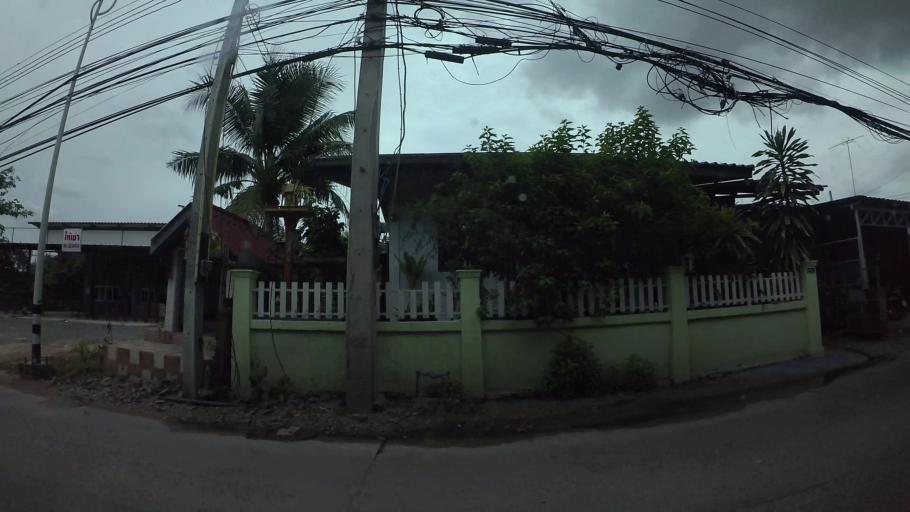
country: TH
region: Chon Buri
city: Si Racha
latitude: 13.1607
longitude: 100.9699
